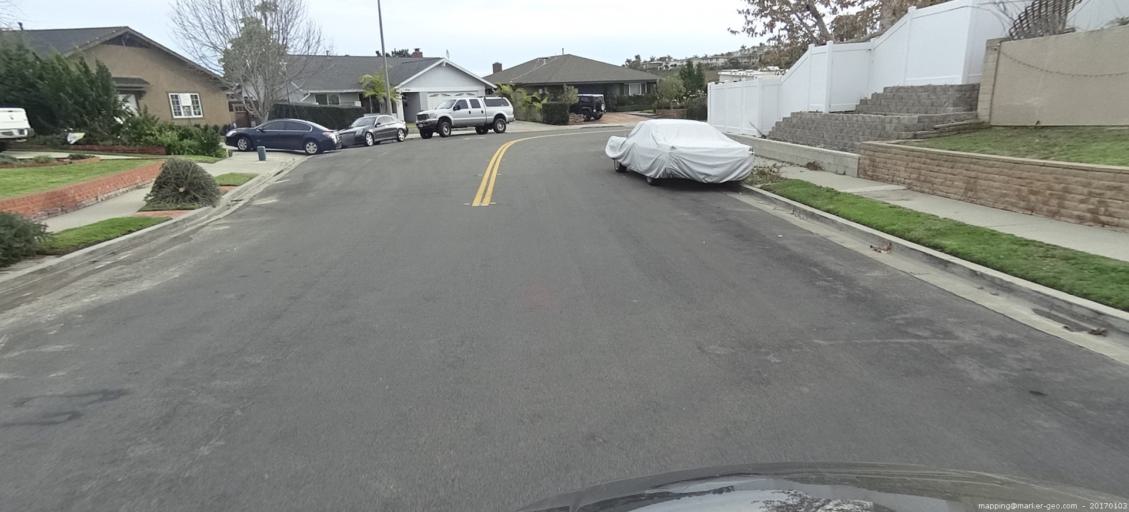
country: US
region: California
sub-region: Orange County
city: Dana Point
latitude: 33.4805
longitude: -117.6922
